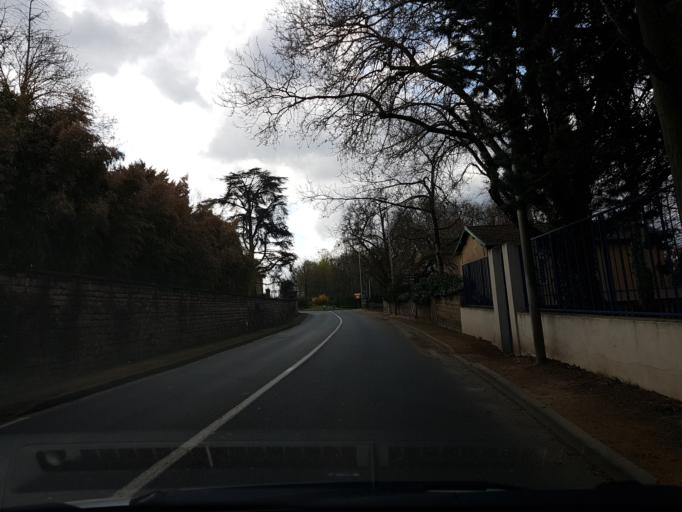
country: FR
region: Rhone-Alpes
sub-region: Departement de l'Ain
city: Trevoux
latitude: 45.9460
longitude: 4.7597
